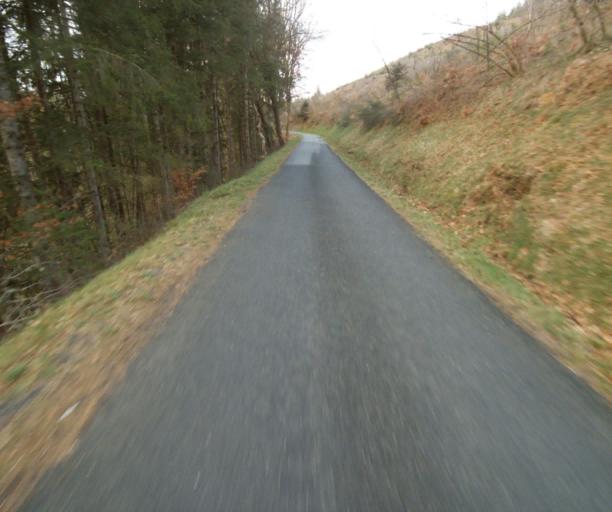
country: FR
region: Limousin
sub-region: Departement de la Correze
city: Correze
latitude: 45.3842
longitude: 1.8891
